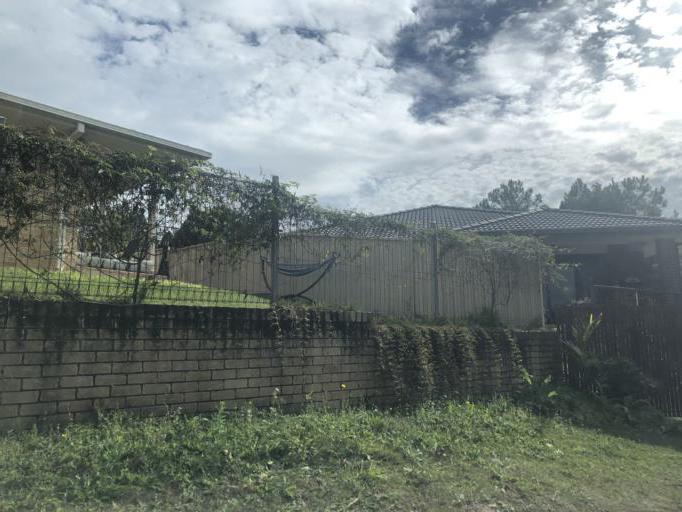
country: AU
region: New South Wales
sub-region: Bellingen
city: Bellingen
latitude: -30.4428
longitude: 152.9019
